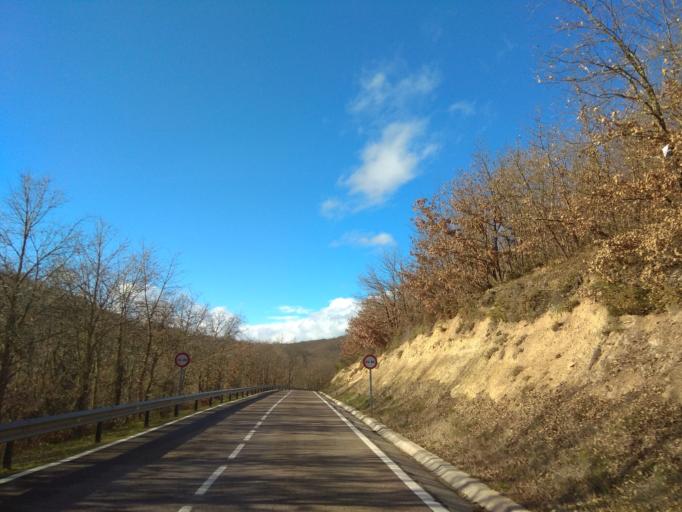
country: ES
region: Cantabria
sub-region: Provincia de Cantabria
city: San Martin de Elines
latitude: 42.9006
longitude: -3.8744
